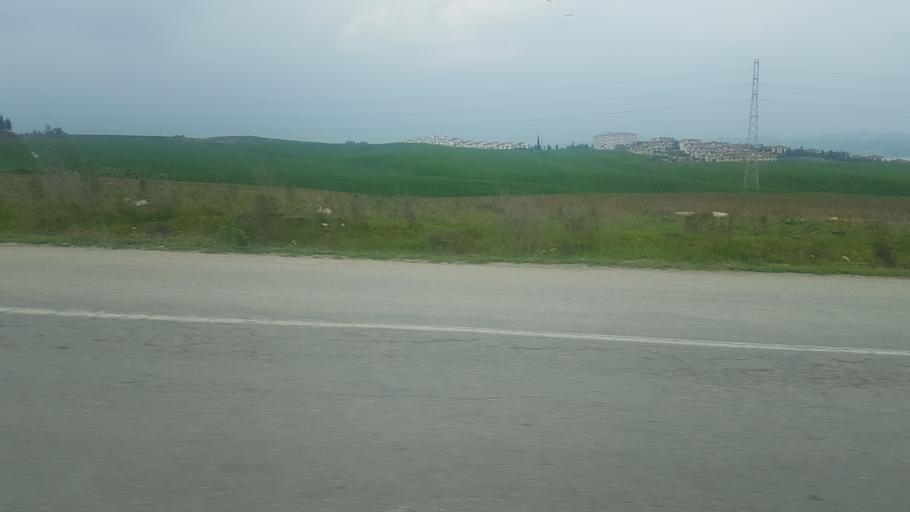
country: TR
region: Adana
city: Seyhan
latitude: 37.0586
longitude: 35.2337
